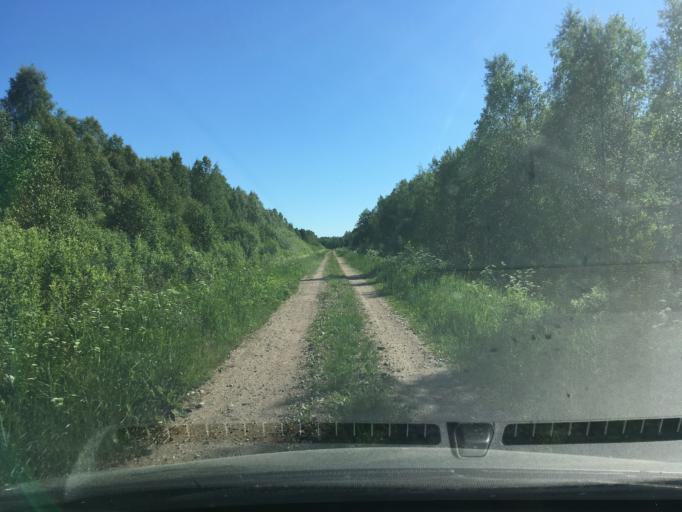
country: EE
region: Laeaene
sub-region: Lihula vald
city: Lihula
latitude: 58.6278
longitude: 23.7305
